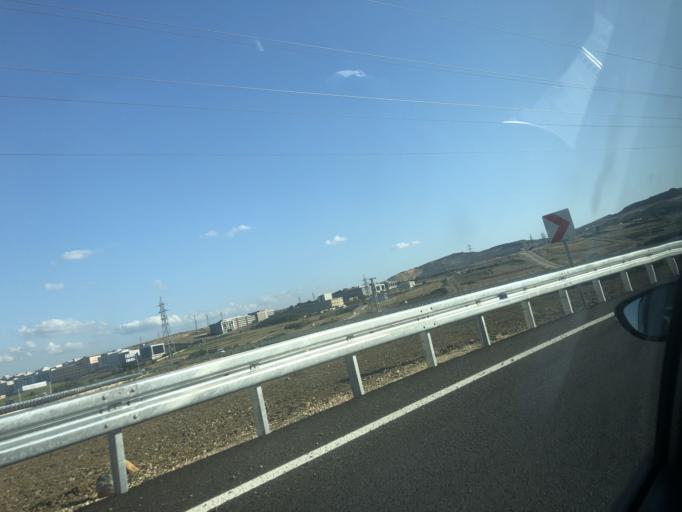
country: TR
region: Istanbul
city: Catalca
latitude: 41.1414
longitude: 28.4803
